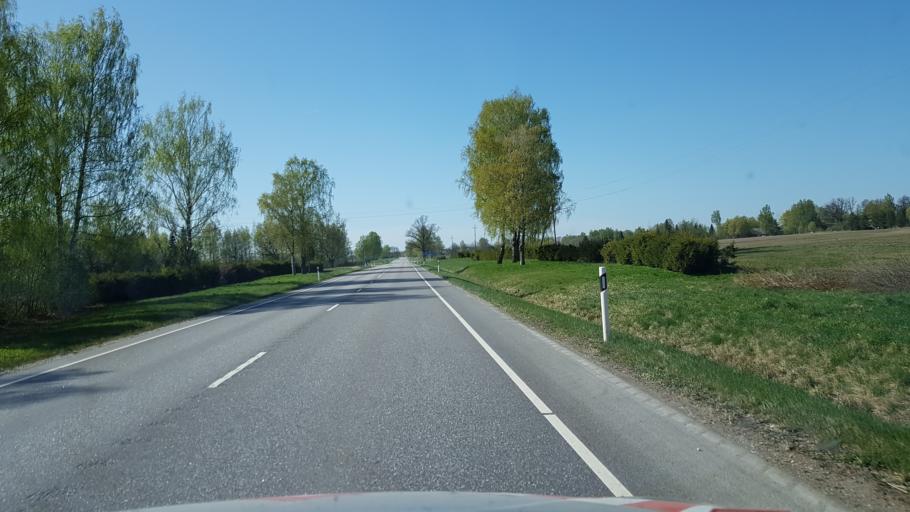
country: EE
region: Viljandimaa
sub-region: Karksi vald
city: Karksi-Nuia
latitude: 58.1085
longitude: 25.5159
